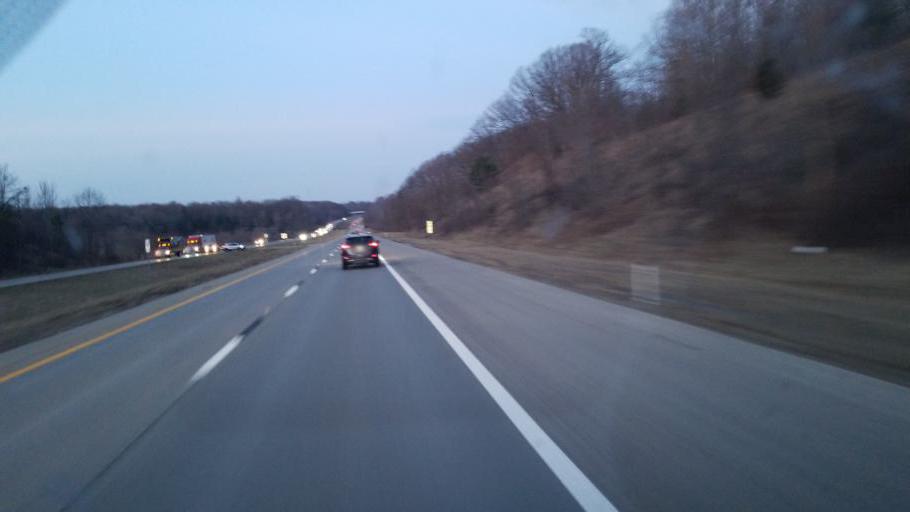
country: US
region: Ohio
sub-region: Lake County
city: Painesville
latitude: 41.6877
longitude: -81.2109
